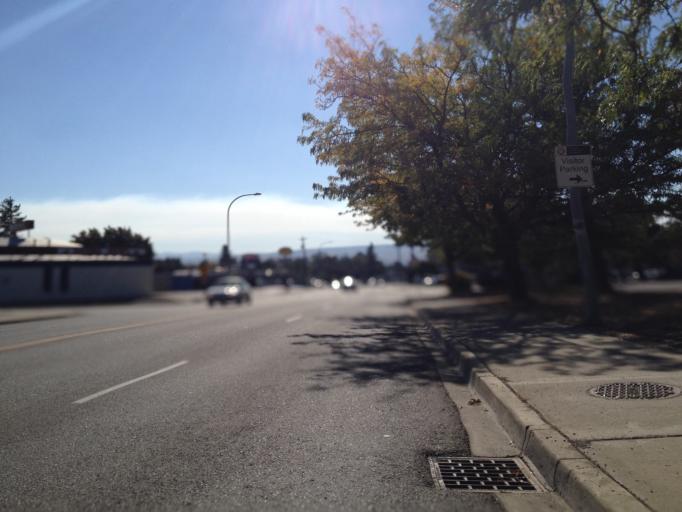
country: US
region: Washington
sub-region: Kittitas County
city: Ellensburg
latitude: 47.0015
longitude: -120.5348
